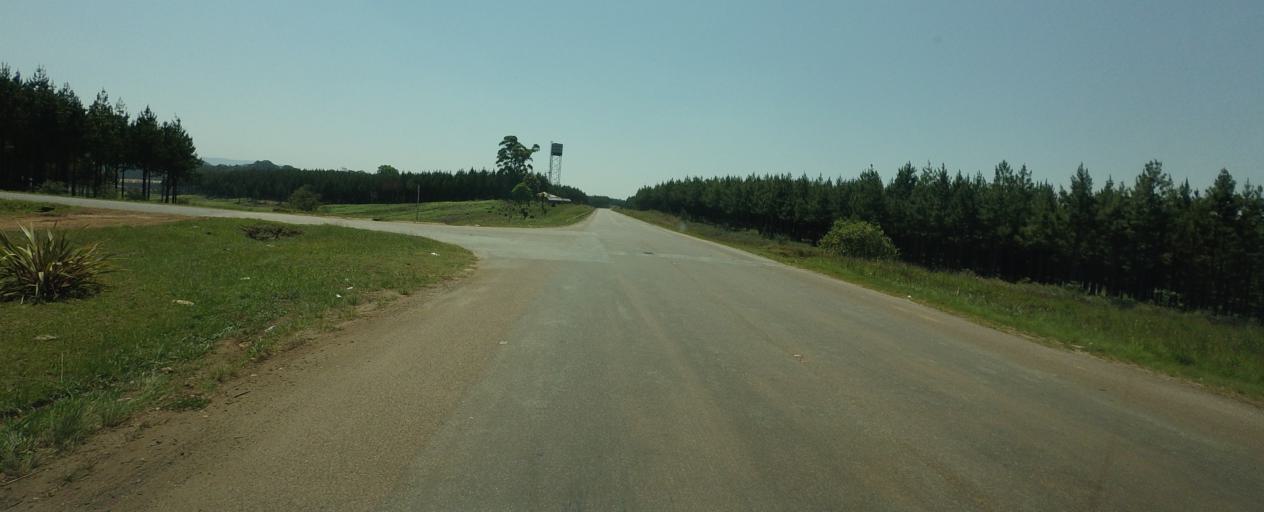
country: ZA
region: Mpumalanga
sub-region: Ehlanzeni District
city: Graksop
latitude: -24.9051
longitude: 30.8450
